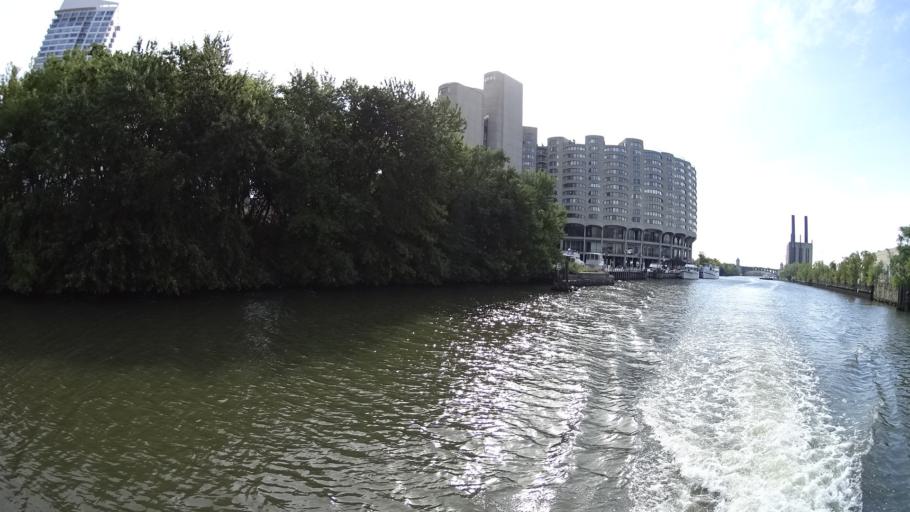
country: US
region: Illinois
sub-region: Cook County
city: Chicago
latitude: 41.8726
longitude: -87.6356
